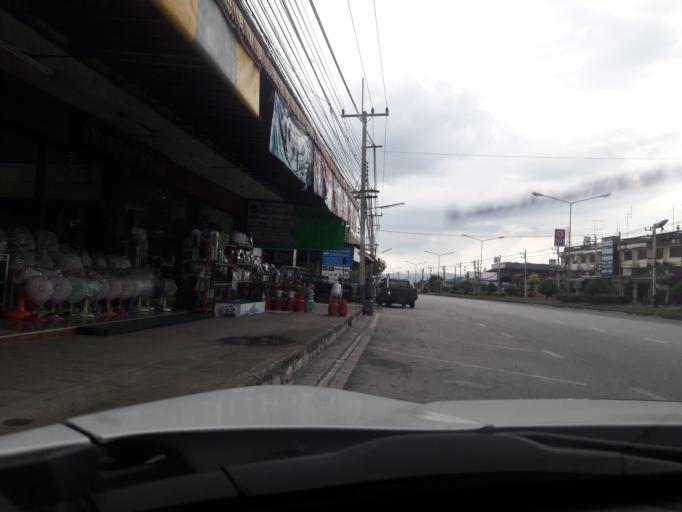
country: TH
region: Lop Buri
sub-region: Amphoe Tha Luang
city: Tha Luang
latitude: 15.0712
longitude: 101.1088
